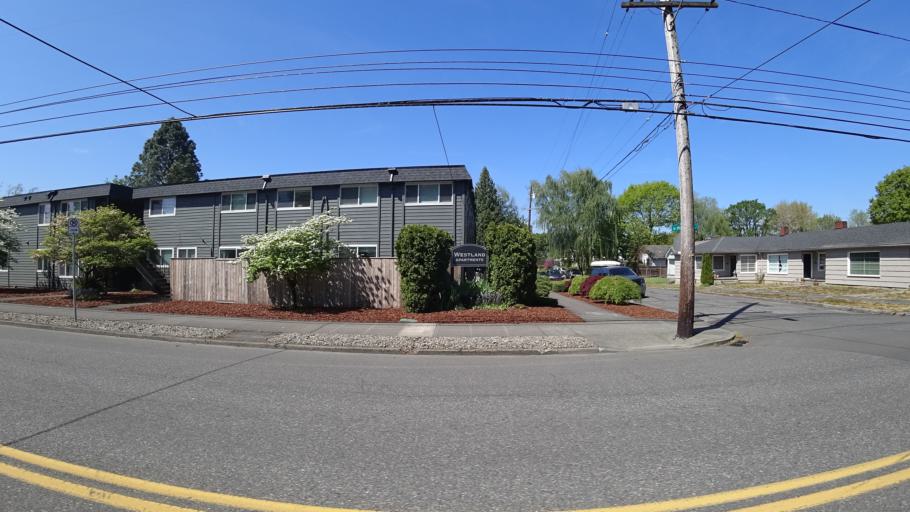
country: US
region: Oregon
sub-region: Clackamas County
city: Milwaukie
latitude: 45.4815
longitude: -122.6496
